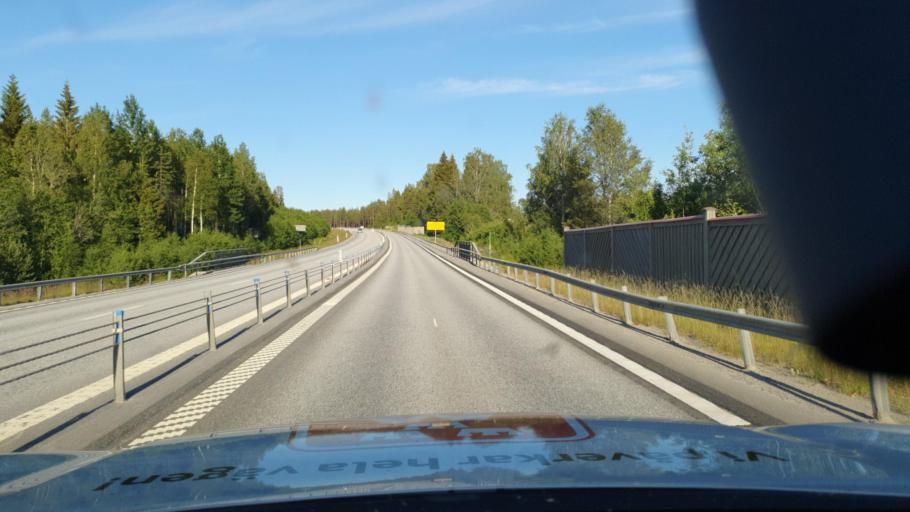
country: SE
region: Vaesterbotten
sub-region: Vannas Kommun
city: Vannasby
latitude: 63.8957
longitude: 19.9262
